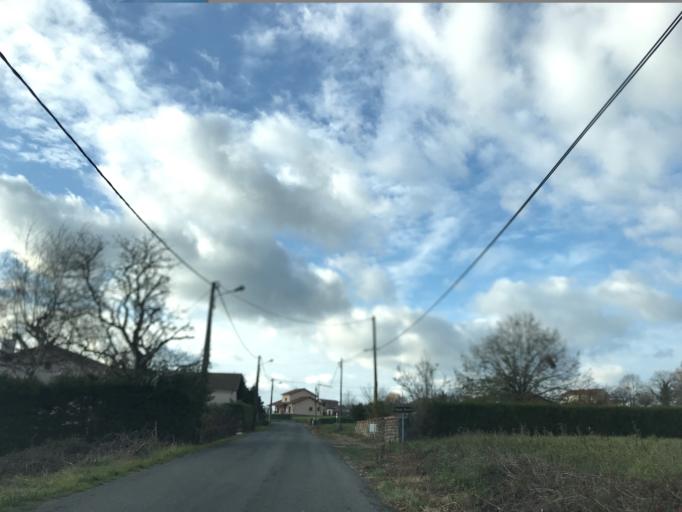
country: FR
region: Auvergne
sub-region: Departement du Puy-de-Dome
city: Courpiere
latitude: 45.7564
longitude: 3.6118
